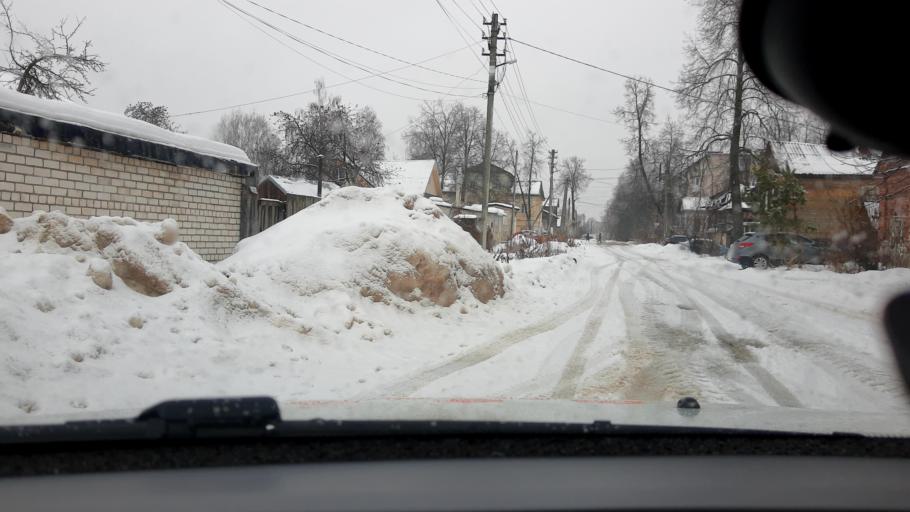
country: RU
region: Nizjnij Novgorod
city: Novaya Balakhna
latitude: 56.4903
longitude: 43.6150
